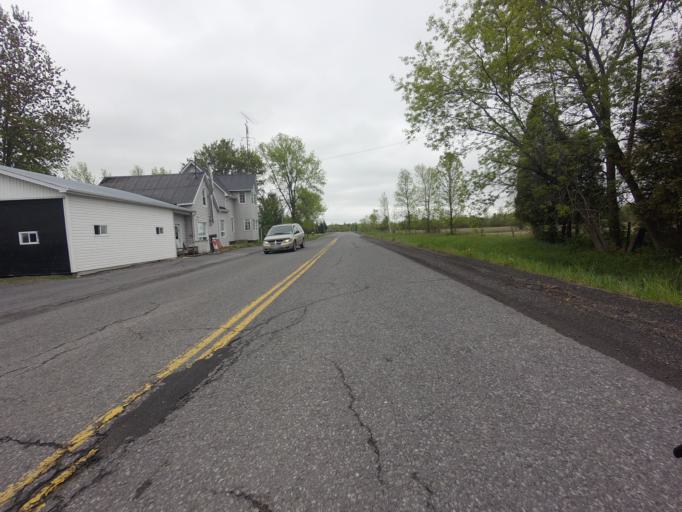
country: US
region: New York
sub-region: St. Lawrence County
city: Norfolk
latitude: 44.9602
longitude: -75.1523
